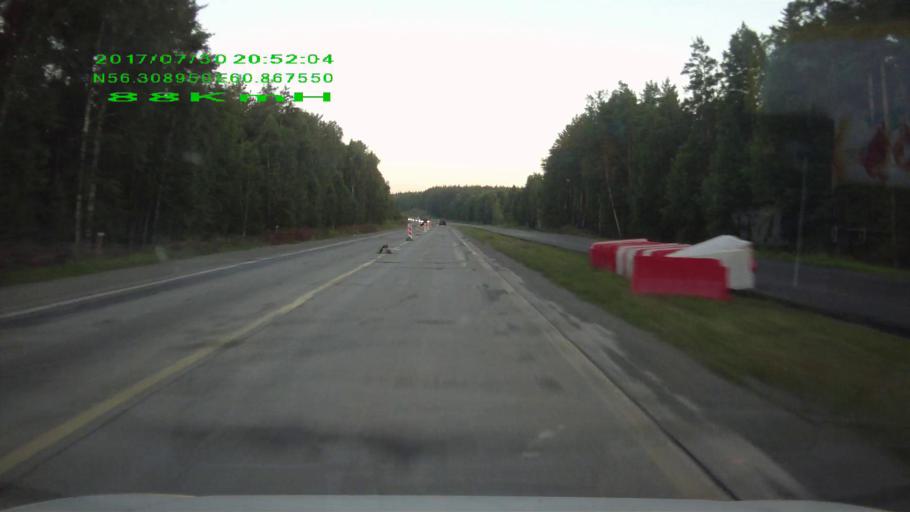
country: RU
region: Sverdlovsk
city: Shchelkun
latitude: 56.3083
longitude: 60.8674
